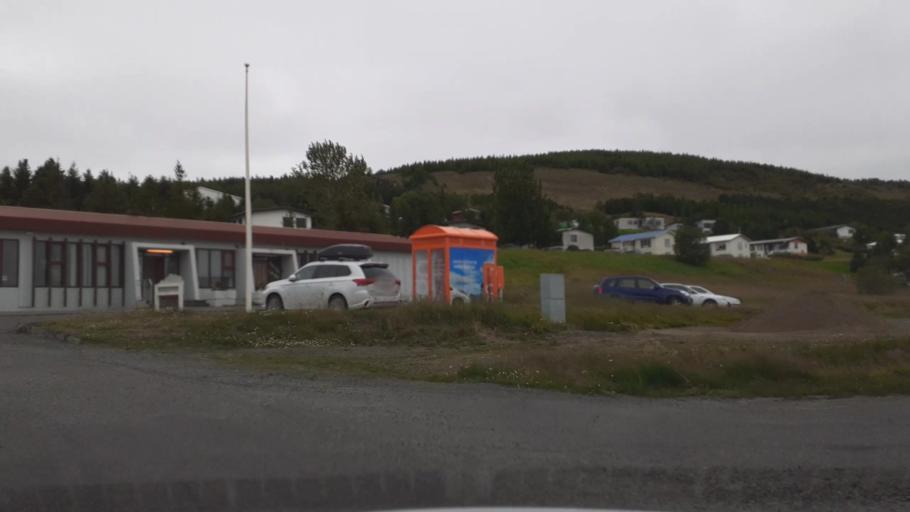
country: IS
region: Northwest
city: Saudarkrokur
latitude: 65.5541
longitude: -19.4466
